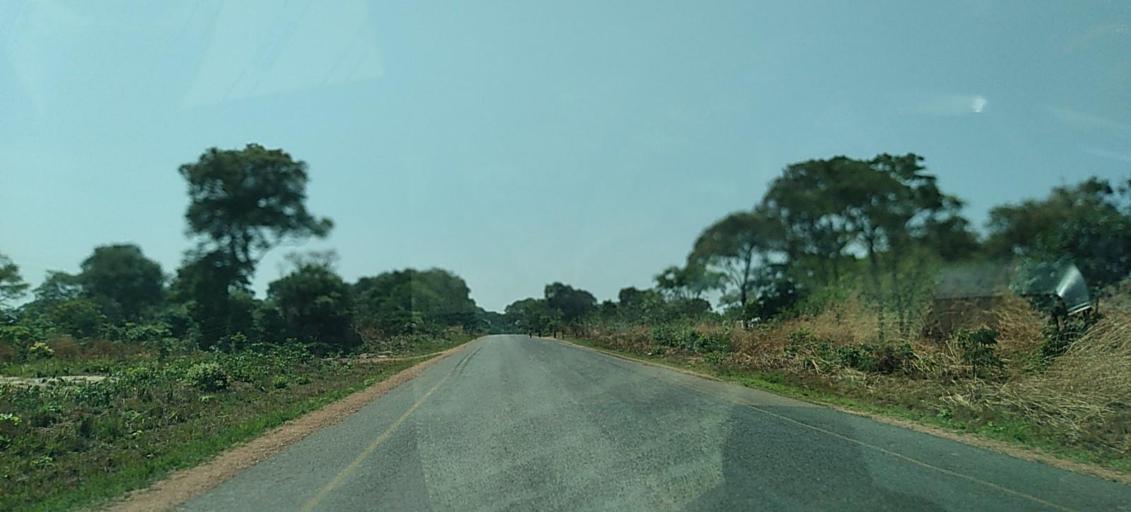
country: ZM
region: North-Western
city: Solwezi
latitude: -12.2965
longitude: 25.8242
